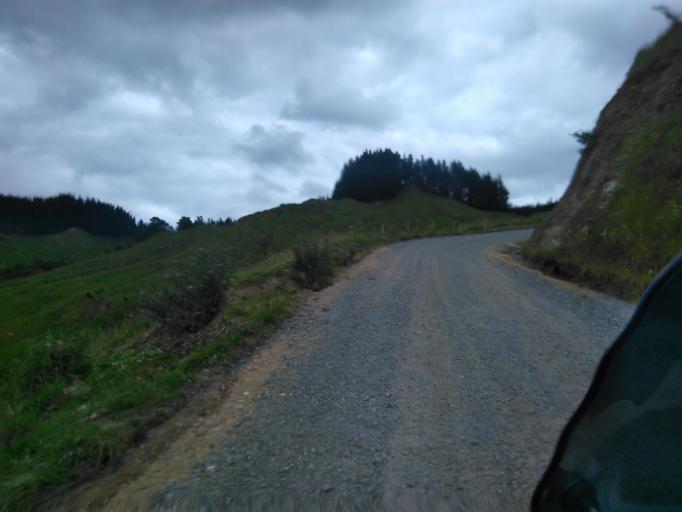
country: NZ
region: Gisborne
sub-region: Gisborne District
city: Gisborne
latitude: -38.0742
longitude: 178.0497
